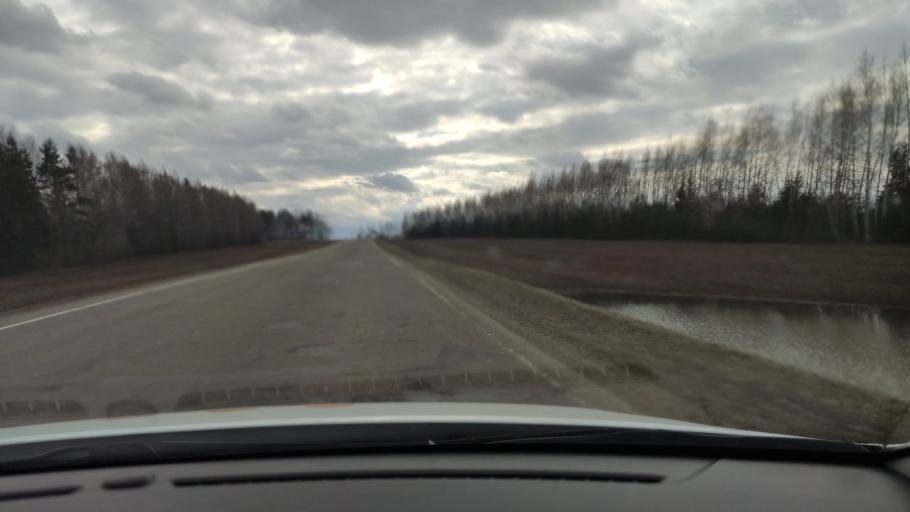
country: RU
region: Tatarstan
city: Vysokaya Gora
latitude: 56.1074
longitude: 49.1776
